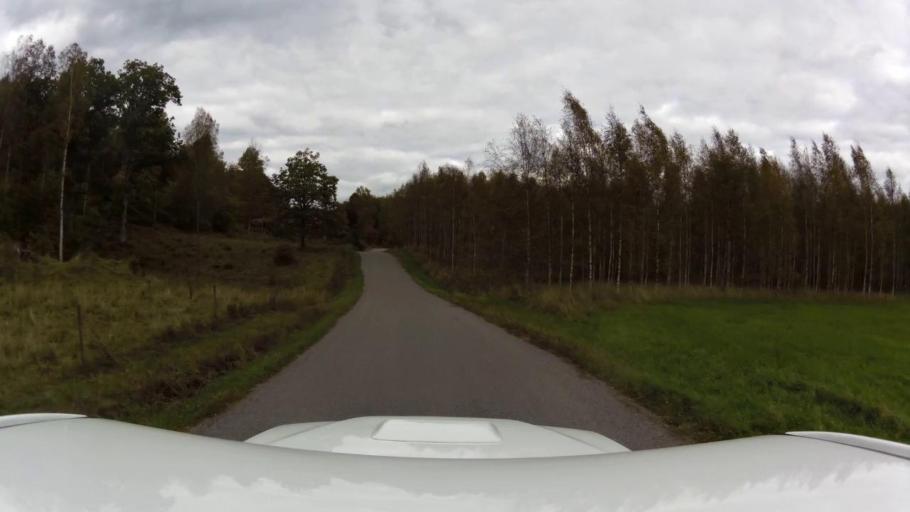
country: SE
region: OEstergoetland
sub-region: Kinda Kommun
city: Rimforsa
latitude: 58.1988
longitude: 15.5619
